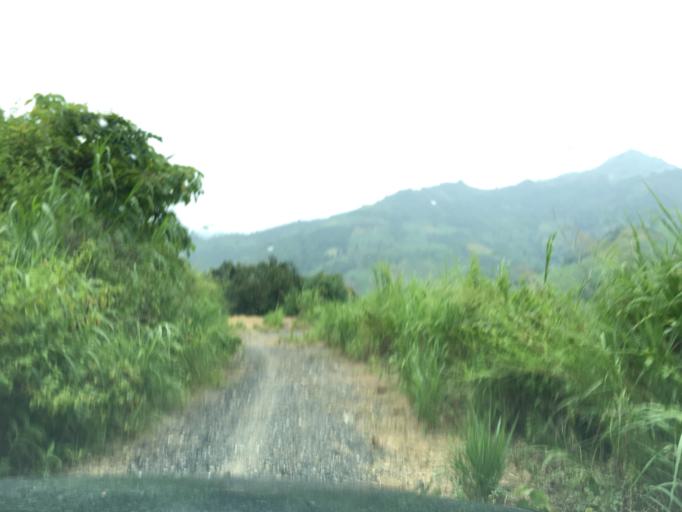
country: CN
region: Guangxi Zhuangzu Zizhiqu
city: Tongle
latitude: 25.0020
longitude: 105.9972
